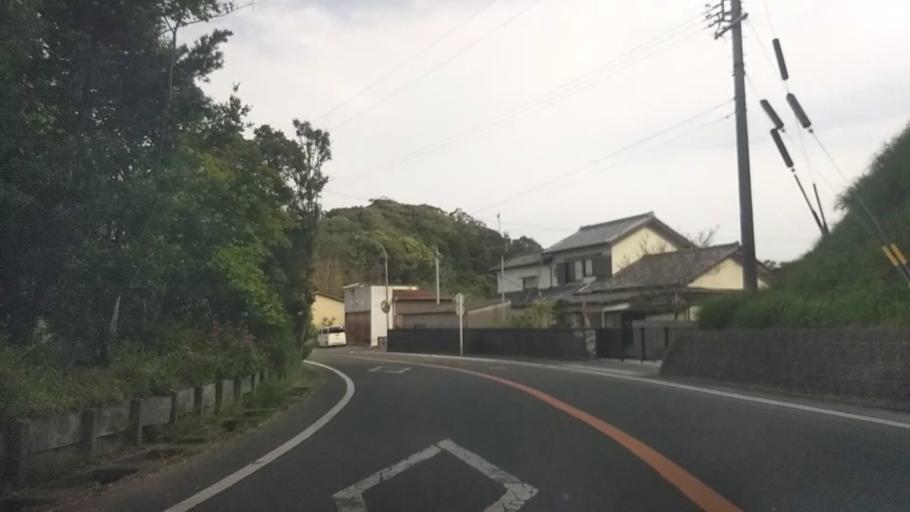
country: JP
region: Shizuoka
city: Kosai-shi
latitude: 34.7124
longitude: 137.6229
